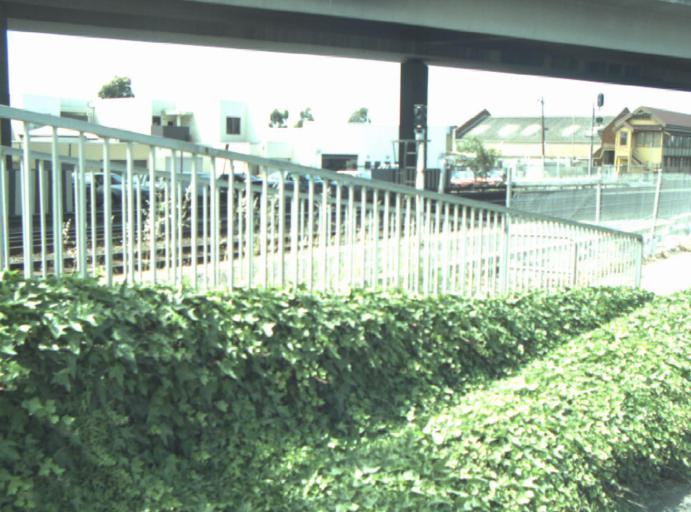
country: AU
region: Victoria
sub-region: Greater Geelong
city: Geelong West
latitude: -38.1393
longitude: 144.3536
